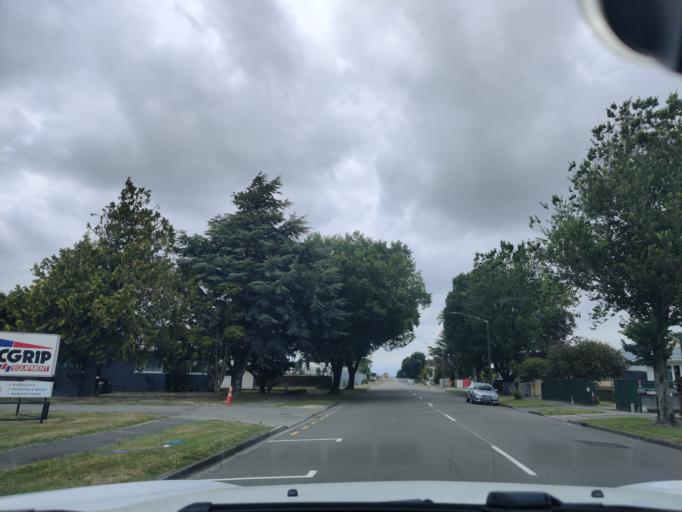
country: NZ
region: Manawatu-Wanganui
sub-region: Palmerston North City
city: Palmerston North
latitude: -40.3501
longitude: 175.5866
